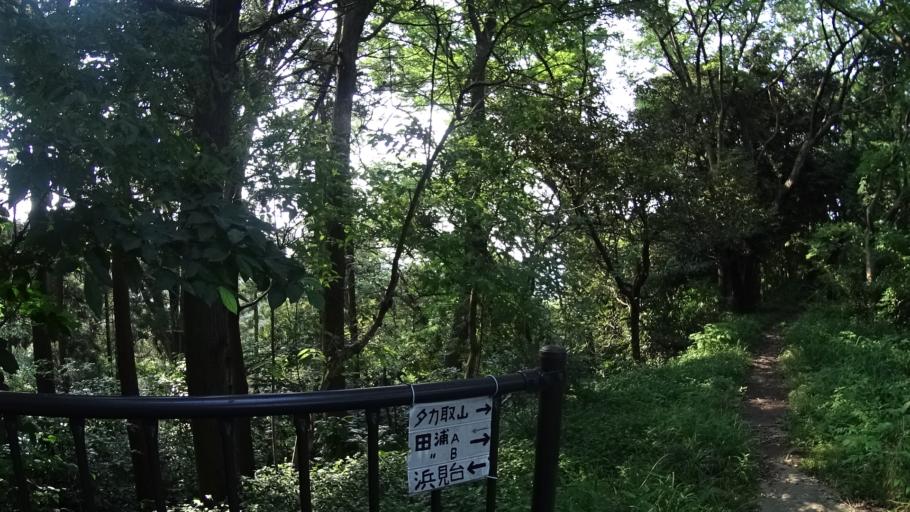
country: JP
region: Kanagawa
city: Zushi
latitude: 35.3045
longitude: 139.6203
